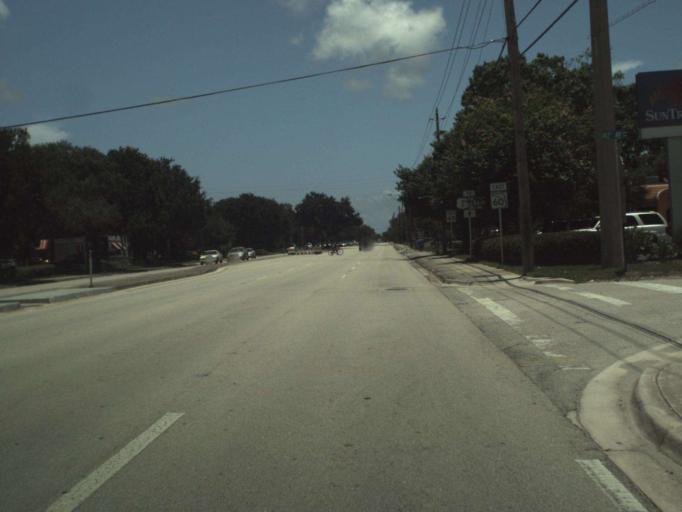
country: US
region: Florida
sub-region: Indian River County
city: Vero Beach South
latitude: 27.6384
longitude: -80.4292
